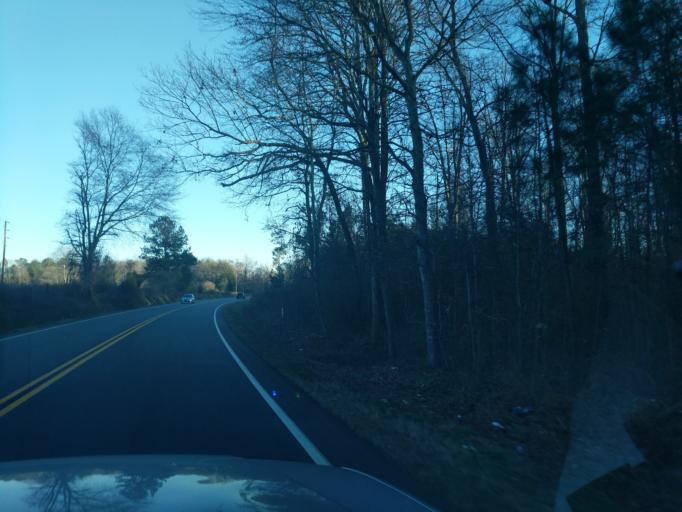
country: US
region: South Carolina
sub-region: Oconee County
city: Utica
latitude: 34.5924
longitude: -82.9580
